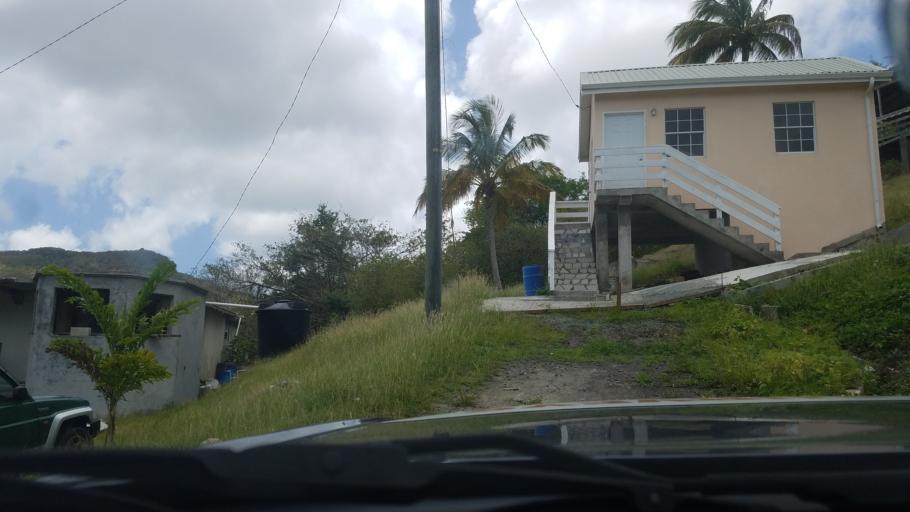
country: LC
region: Gros-Islet
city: Gros Islet
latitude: 14.0567
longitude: -60.9315
